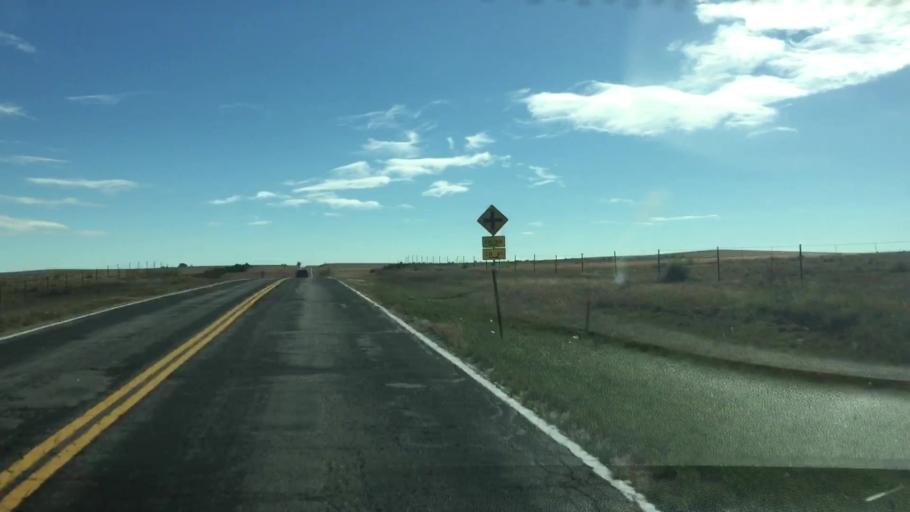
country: US
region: Colorado
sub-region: Elbert County
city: Kiowa
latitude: 39.2736
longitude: -104.2373
